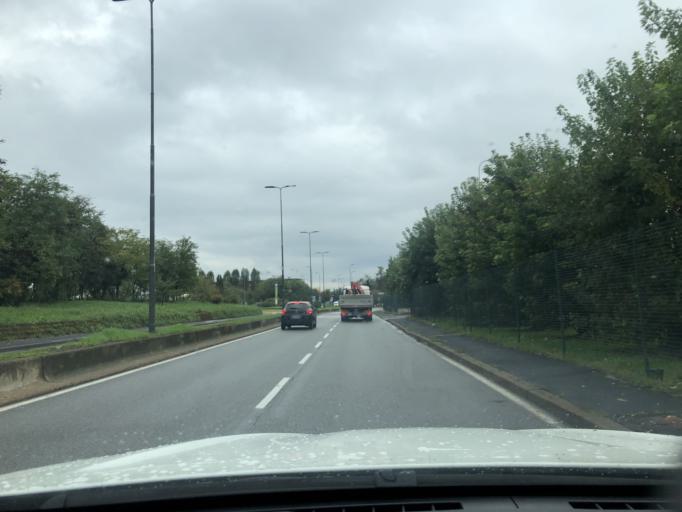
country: IT
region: Lombardy
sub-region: Citta metropolitana di Milano
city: Settimo Milanese
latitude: 45.4598
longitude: 9.0686
